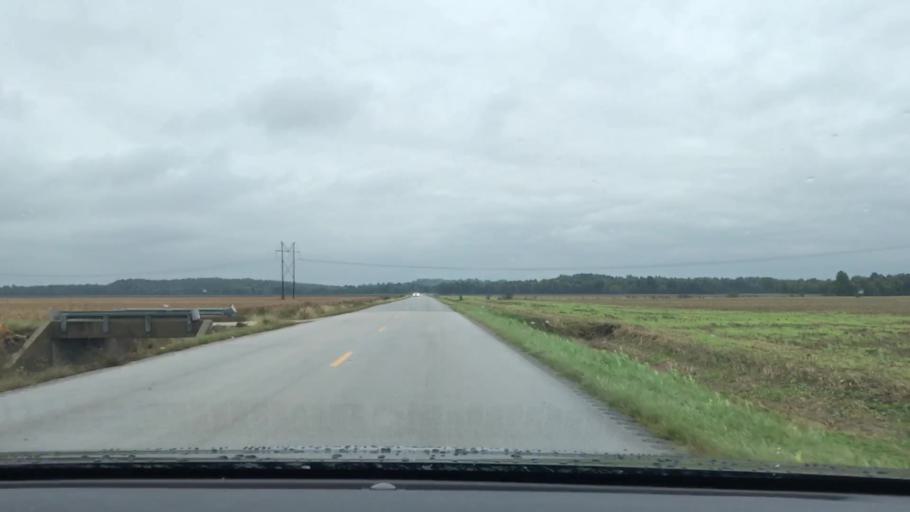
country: US
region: Kentucky
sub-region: McLean County
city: Calhoun
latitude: 37.5066
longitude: -87.2507
